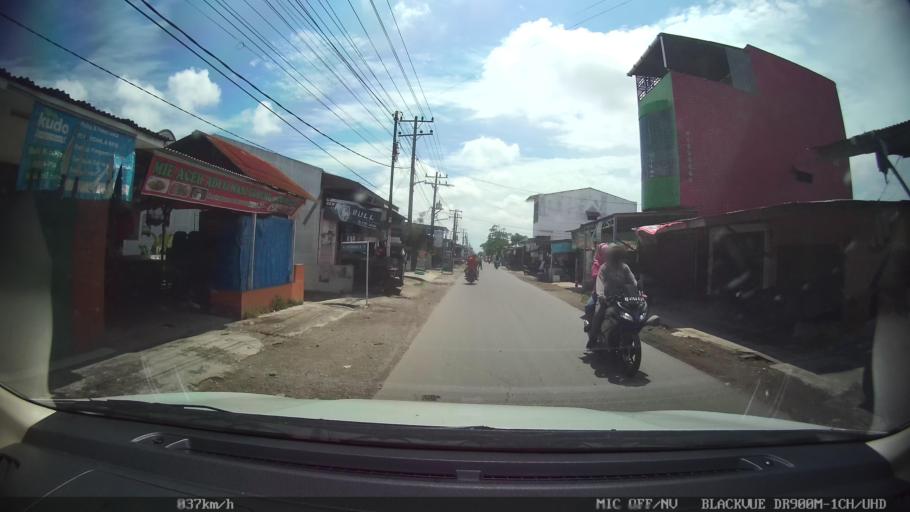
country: ID
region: North Sumatra
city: Medan
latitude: 3.6020
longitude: 98.7597
